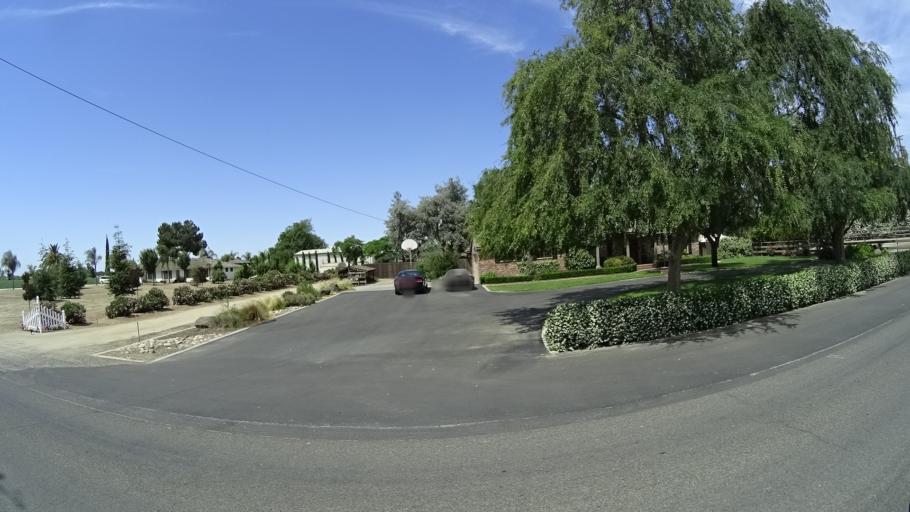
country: US
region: California
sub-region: Kings County
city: Armona
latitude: 36.3494
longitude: -119.6910
